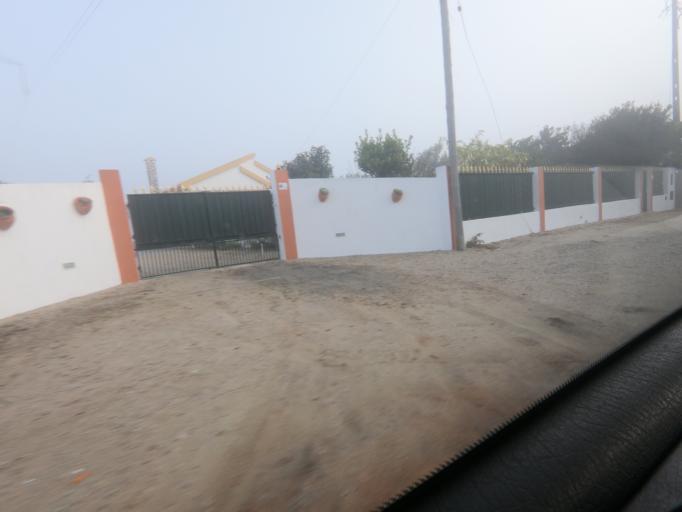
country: PT
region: Setubal
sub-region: Palmela
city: Palmela
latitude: 38.6077
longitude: -8.8580
